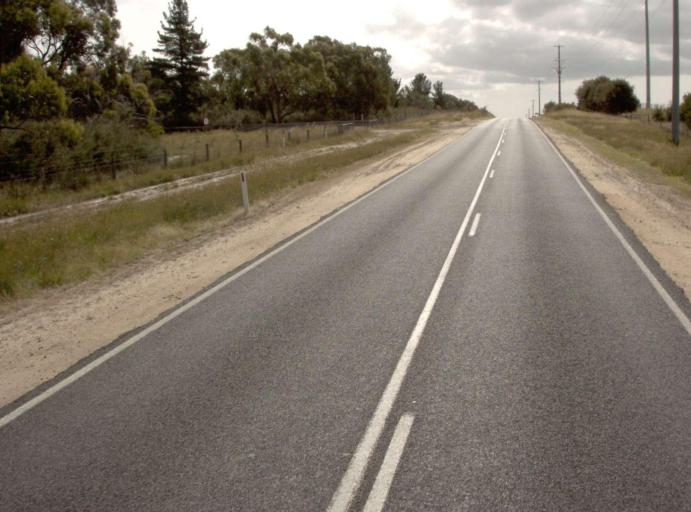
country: AU
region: Victoria
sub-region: Wellington
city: Sale
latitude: -38.2194
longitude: 147.1562
